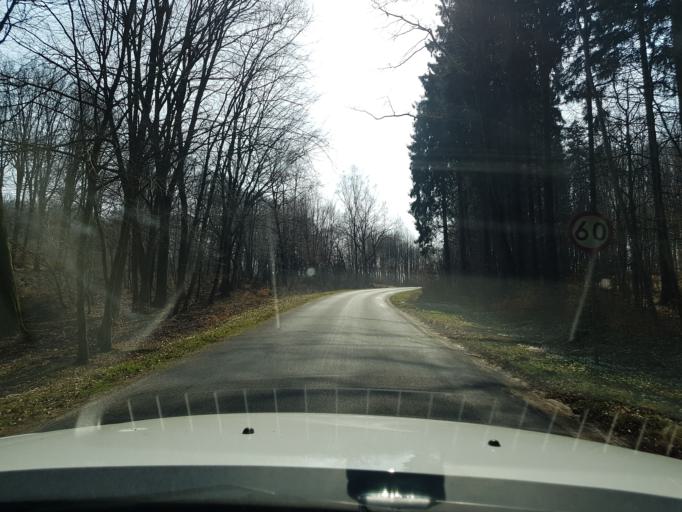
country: PL
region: West Pomeranian Voivodeship
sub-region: Powiat koszalinski
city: Sianow
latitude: 54.2586
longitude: 16.3137
